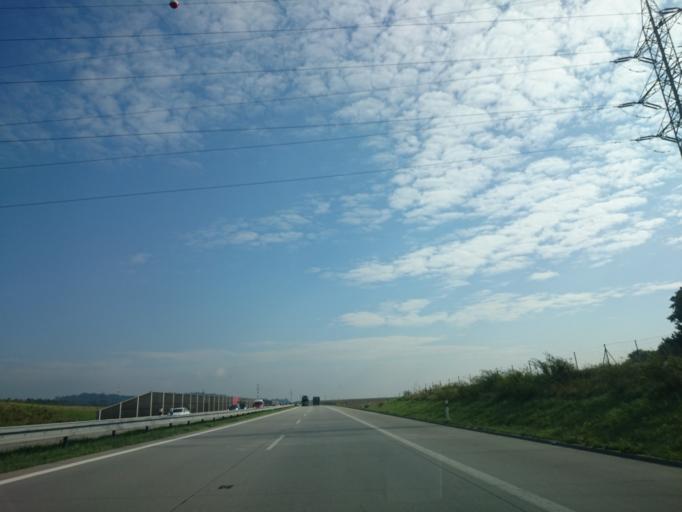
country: CZ
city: Bilovec
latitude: 49.7104
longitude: 17.9974
